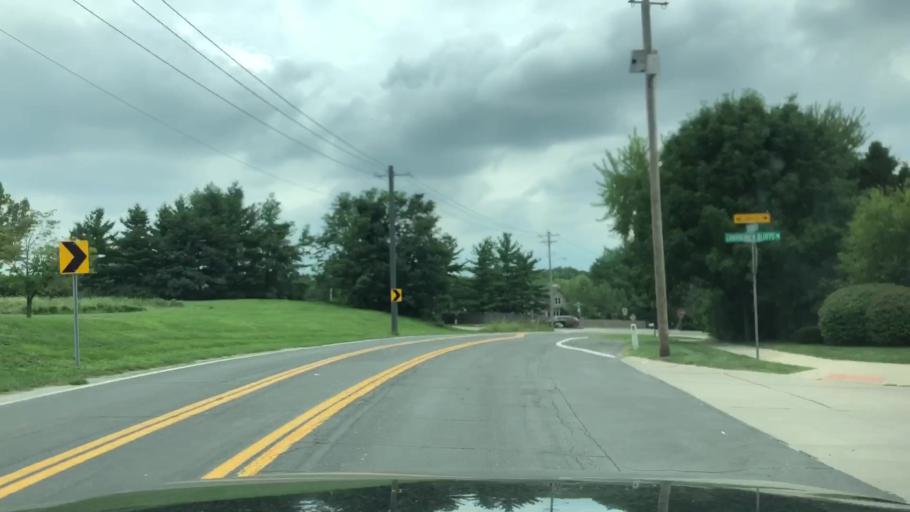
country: US
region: Missouri
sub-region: Saint Louis County
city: Hazelwood
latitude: 38.8095
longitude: -90.3798
